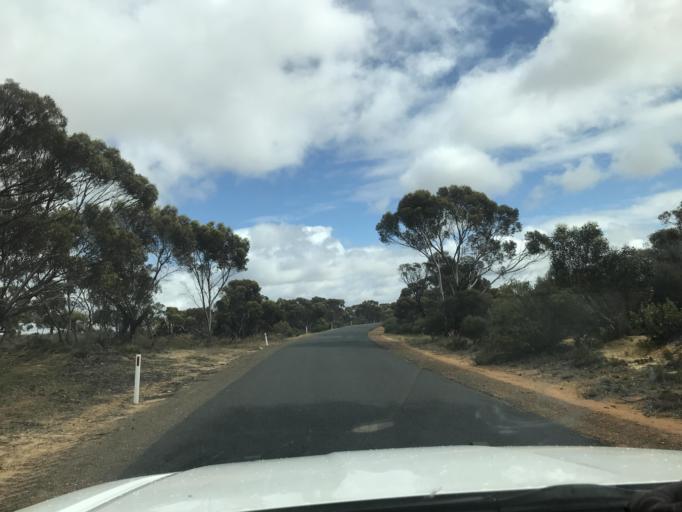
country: AU
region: South Australia
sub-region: Tatiara
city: Bordertown
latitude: -36.1753
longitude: 141.1522
